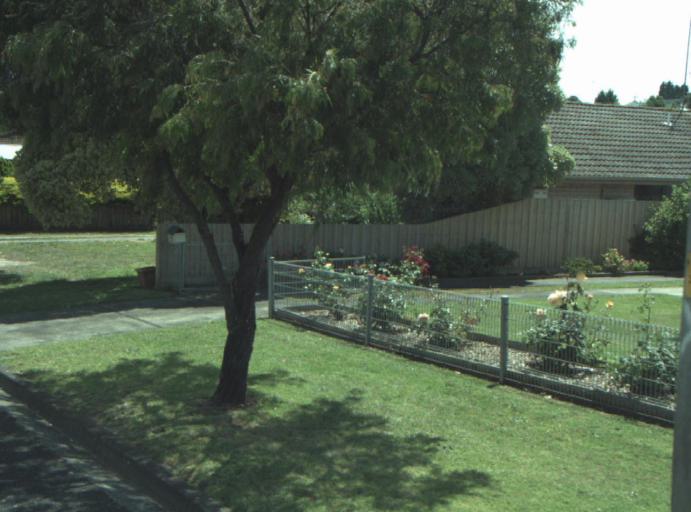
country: AU
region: Victoria
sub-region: Greater Geelong
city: Clifton Springs
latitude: -38.1560
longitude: 144.5765
